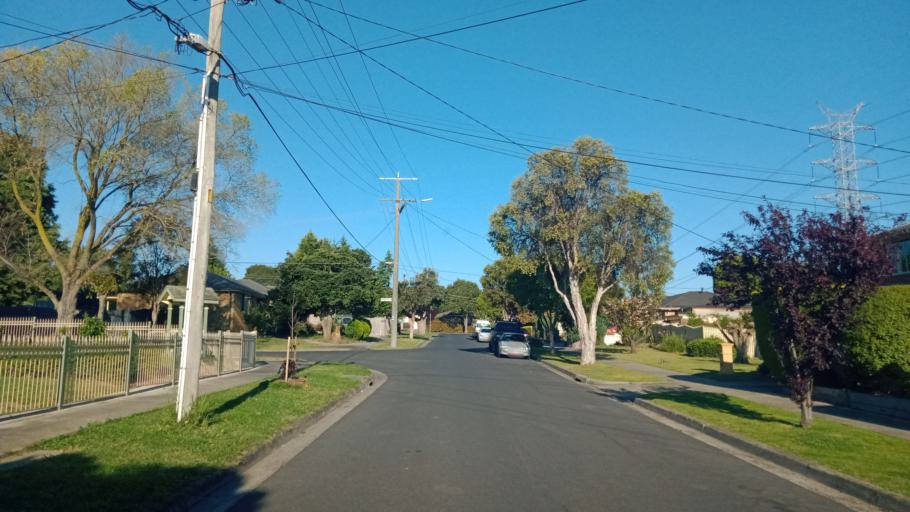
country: AU
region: Victoria
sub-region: Monash
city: Mulgrave
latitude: -37.9279
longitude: 145.1787
